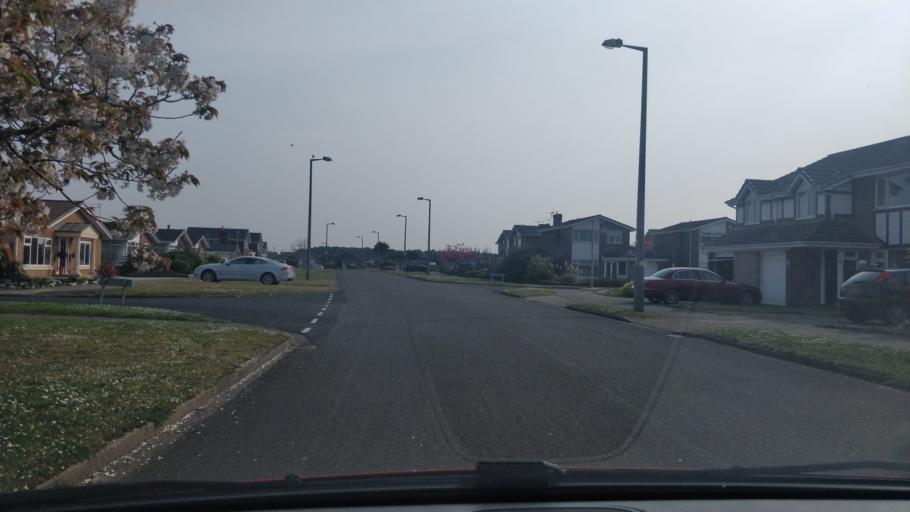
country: GB
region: England
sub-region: Sefton
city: Formby
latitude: 53.6023
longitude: -3.0535
